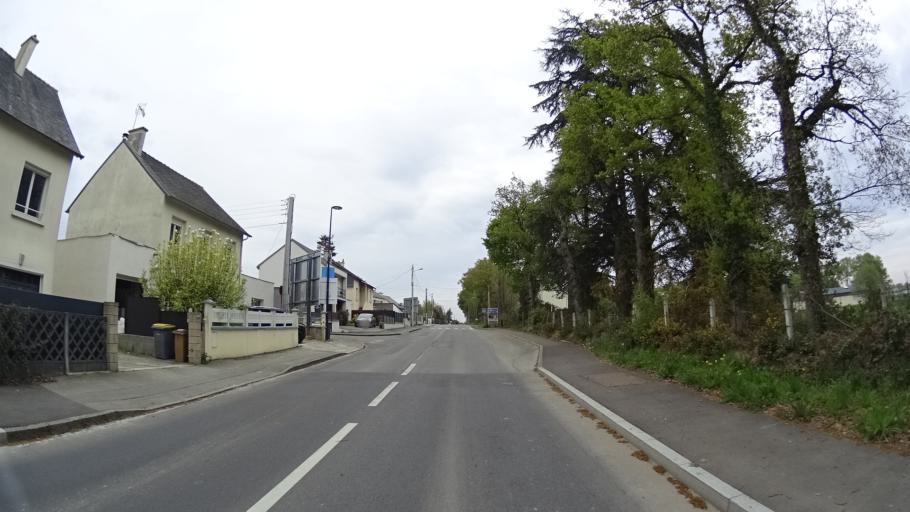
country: FR
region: Brittany
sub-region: Departement d'Ille-et-Vilaine
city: Bruz
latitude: 48.0322
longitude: -1.7515
